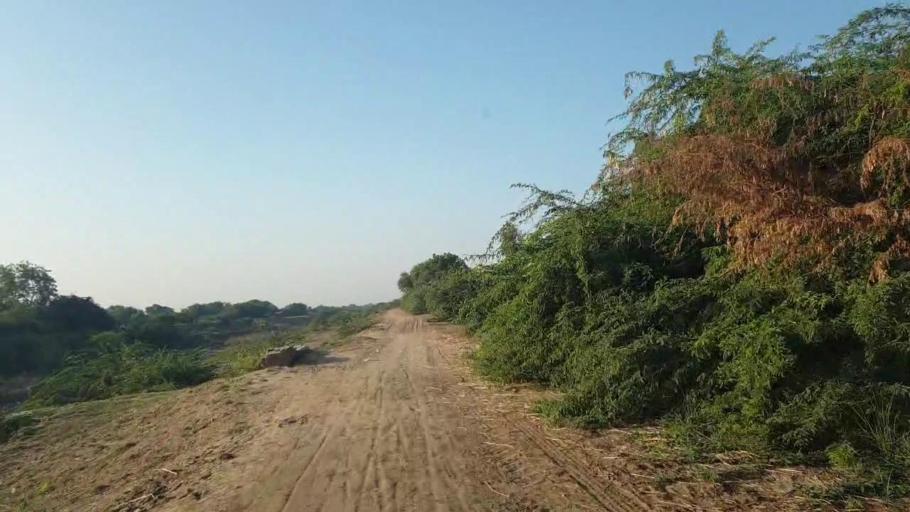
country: PK
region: Sindh
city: Badin
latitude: 24.6177
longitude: 68.7880
